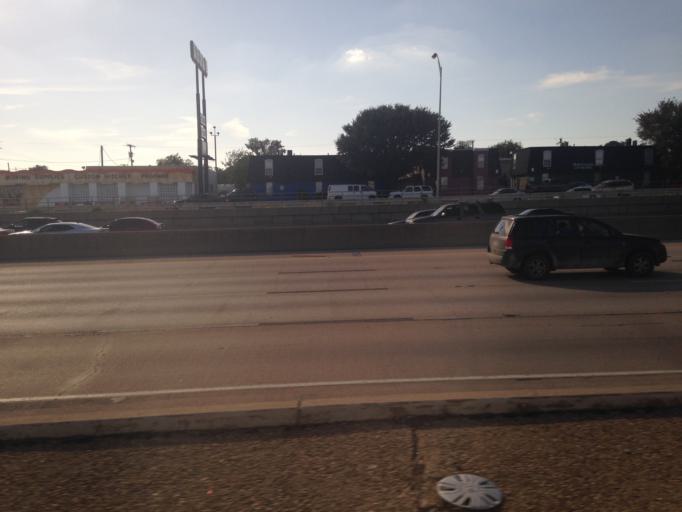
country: US
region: Texas
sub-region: Tarrant County
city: Fort Worth
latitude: 32.7076
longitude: -97.3203
